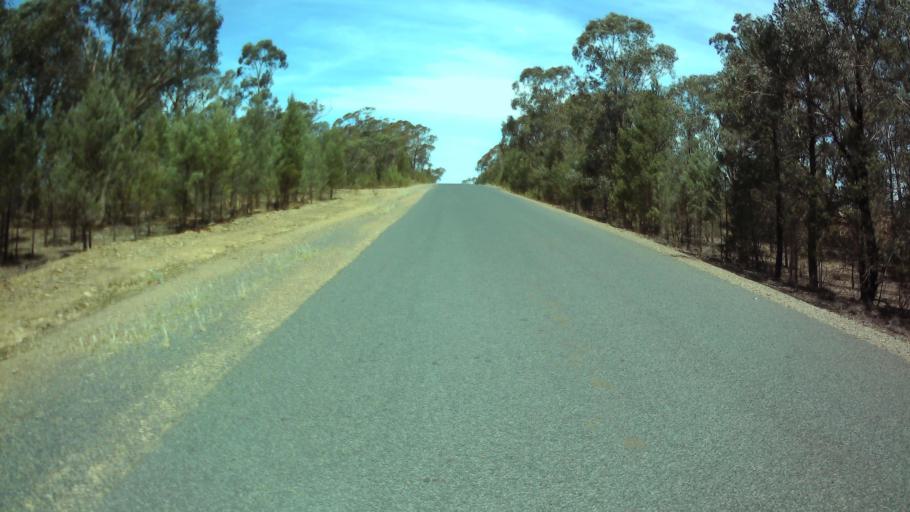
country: AU
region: New South Wales
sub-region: Weddin
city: Grenfell
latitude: -33.9005
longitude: 147.7552
